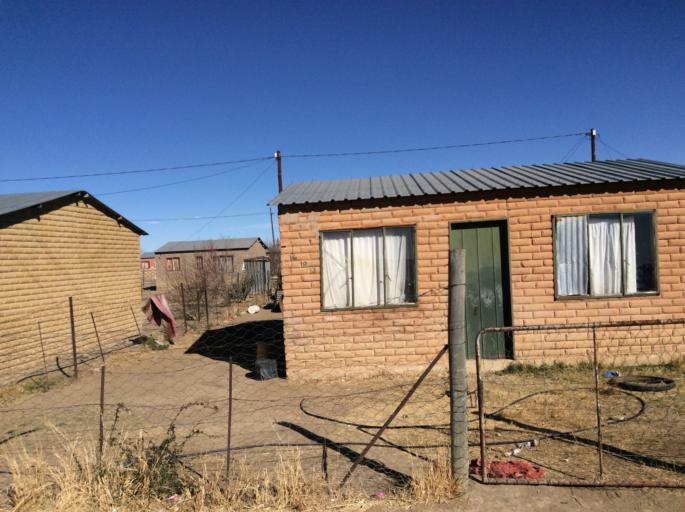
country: ZA
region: Orange Free State
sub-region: Lejweleputswa District Municipality
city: Brandfort
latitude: -28.7333
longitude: 26.1045
